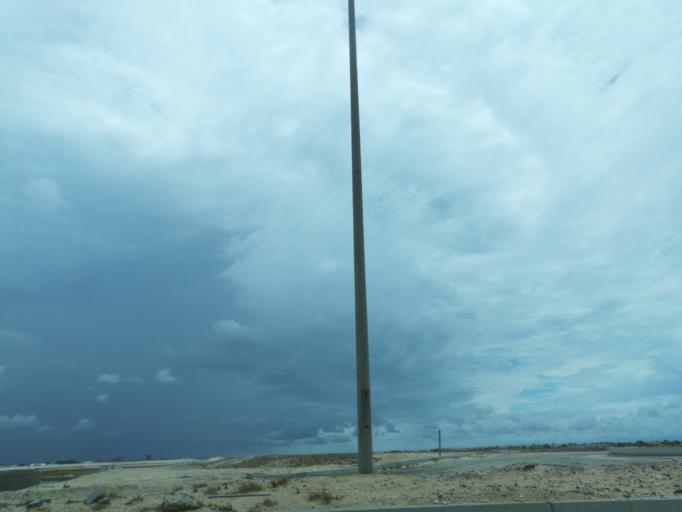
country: NG
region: Lagos
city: Ikoyi
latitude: 6.4090
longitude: 3.4267
